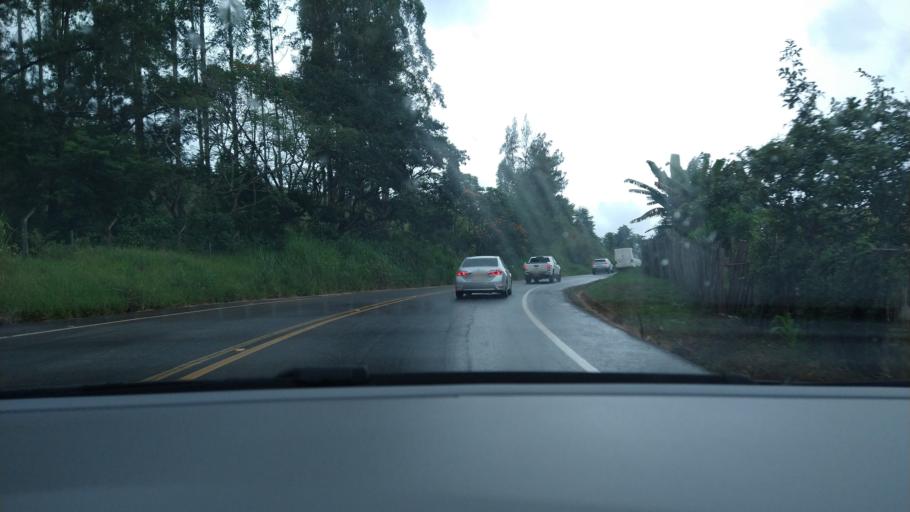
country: BR
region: Minas Gerais
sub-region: Vicosa
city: Vicosa
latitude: -20.6475
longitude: -42.8657
